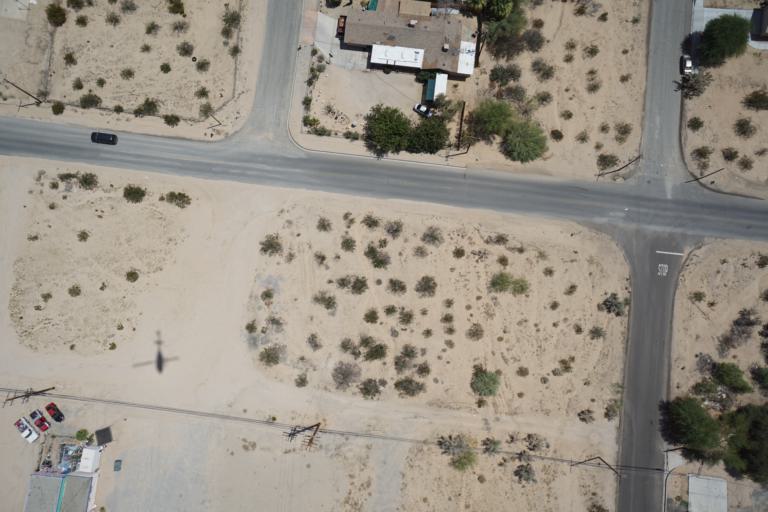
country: US
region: California
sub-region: San Bernardino County
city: Twentynine Palms
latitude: 34.1454
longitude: -116.0533
